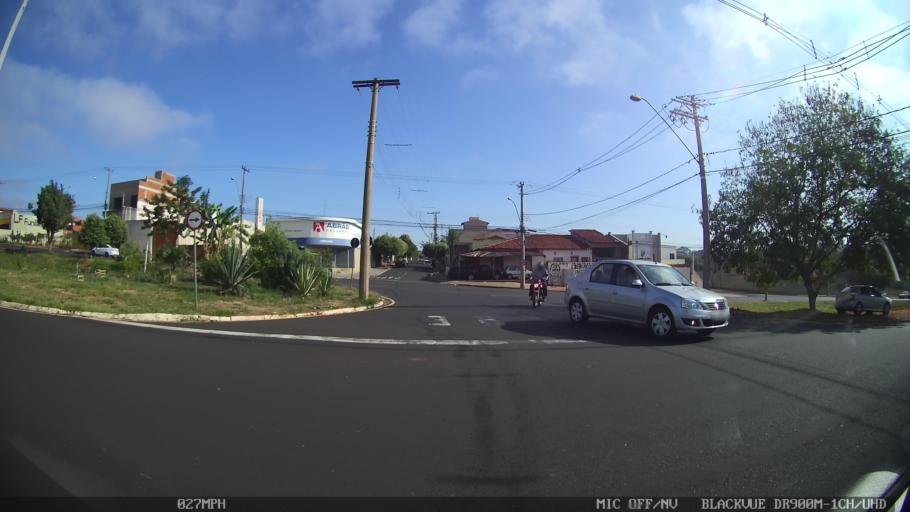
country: BR
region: Sao Paulo
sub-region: Sao Jose Do Rio Preto
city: Sao Jose do Rio Preto
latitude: -20.7972
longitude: -49.4279
